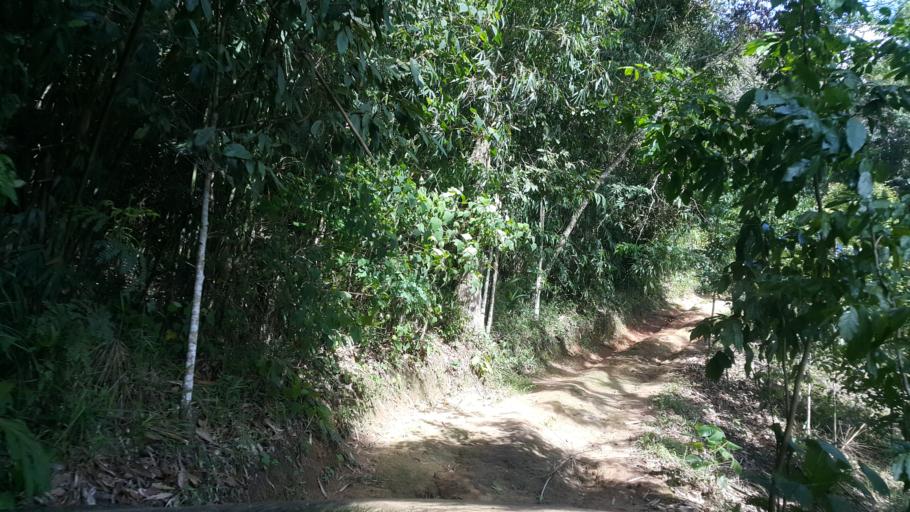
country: TH
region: Loei
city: Na Haeo
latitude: 17.5541
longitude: 100.9563
